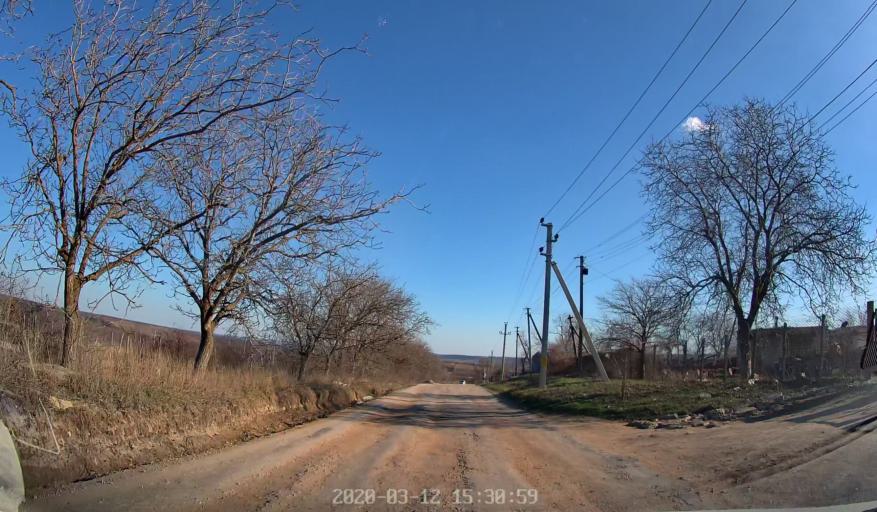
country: MD
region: Chisinau
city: Ciorescu
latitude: 47.1589
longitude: 28.9411
